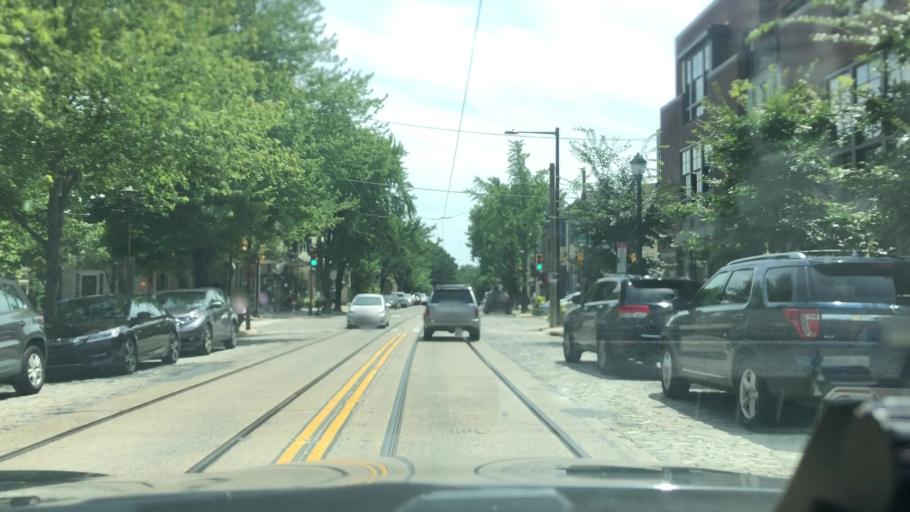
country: US
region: Pennsylvania
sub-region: Montgomery County
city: Wyndmoor
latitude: 40.0735
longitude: -75.2032
